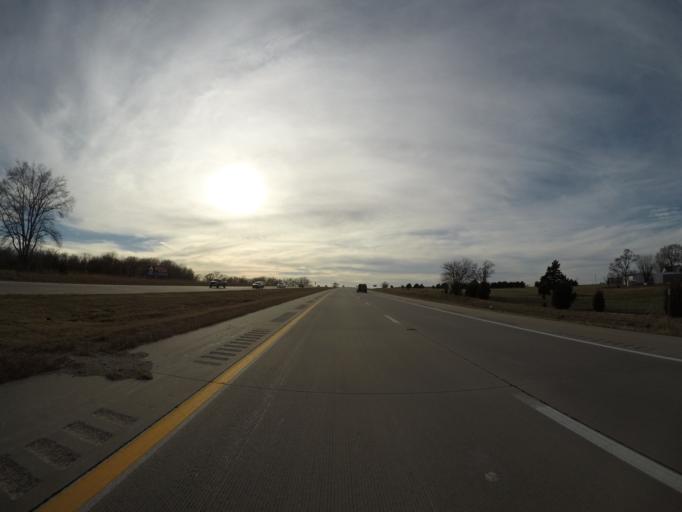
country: US
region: Kansas
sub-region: Franklin County
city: Wellsville
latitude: 38.7085
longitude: -95.0617
